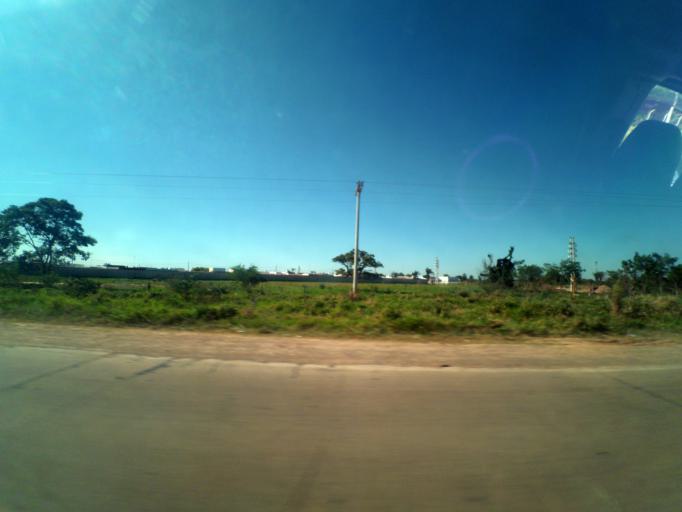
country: BO
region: Santa Cruz
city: Santa Cruz de la Sierra
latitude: -17.7622
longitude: -63.2339
